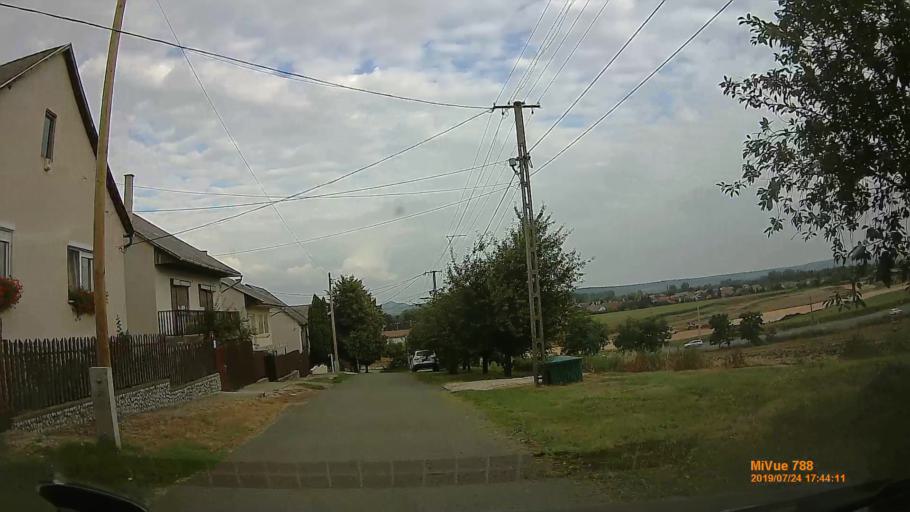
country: HU
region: Borsod-Abauj-Zemplen
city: Encs
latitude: 48.3366
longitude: 21.1052
